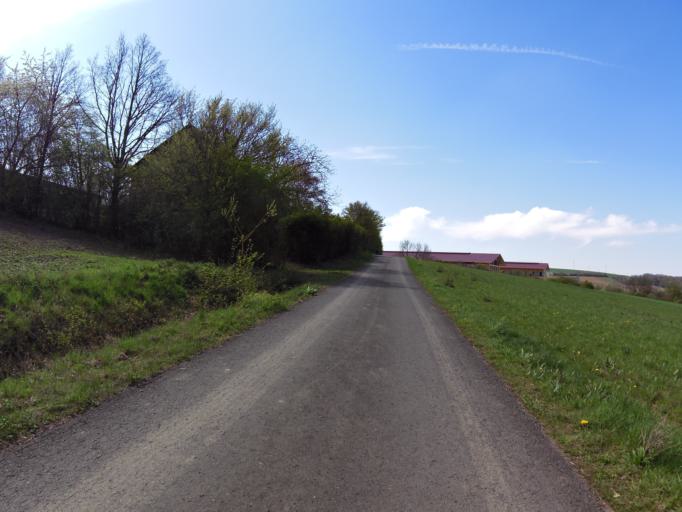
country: DE
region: Bavaria
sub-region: Regierungsbezirk Unterfranken
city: Rottendorf
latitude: 49.7896
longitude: 10.0399
